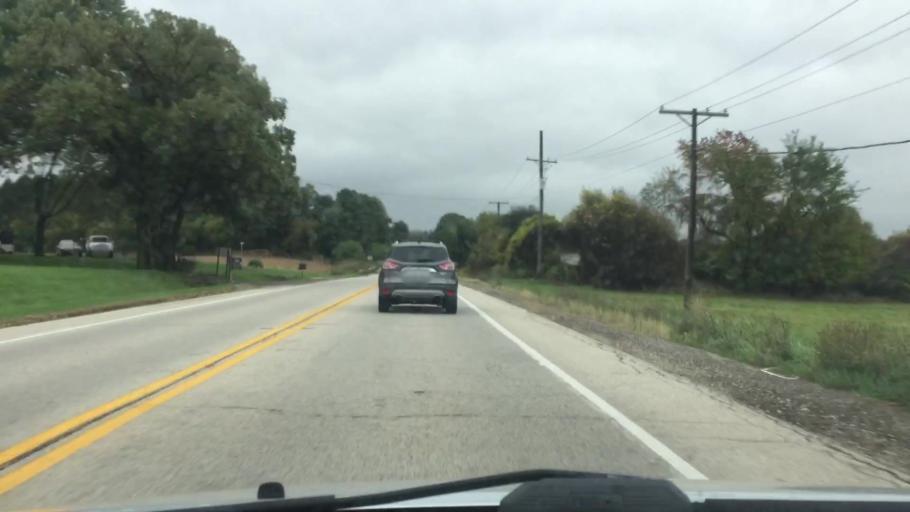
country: US
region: Illinois
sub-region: McHenry County
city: McCullom Lake
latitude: 42.3891
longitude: -88.2872
